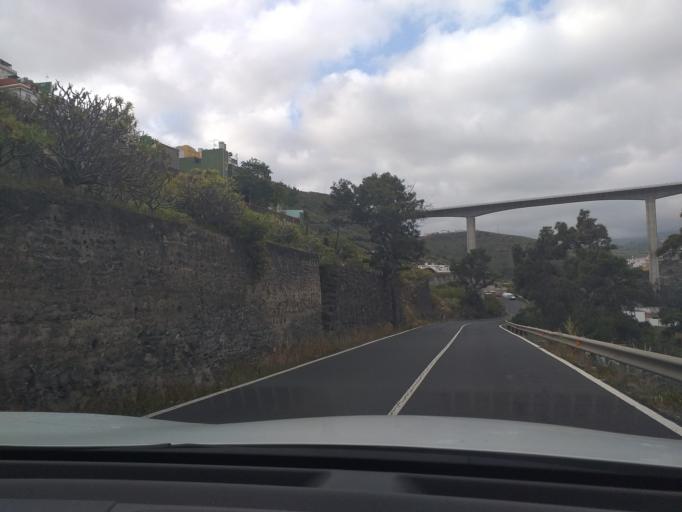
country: ES
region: Canary Islands
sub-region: Provincia de Las Palmas
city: Arucas
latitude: 28.1136
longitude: -15.4961
